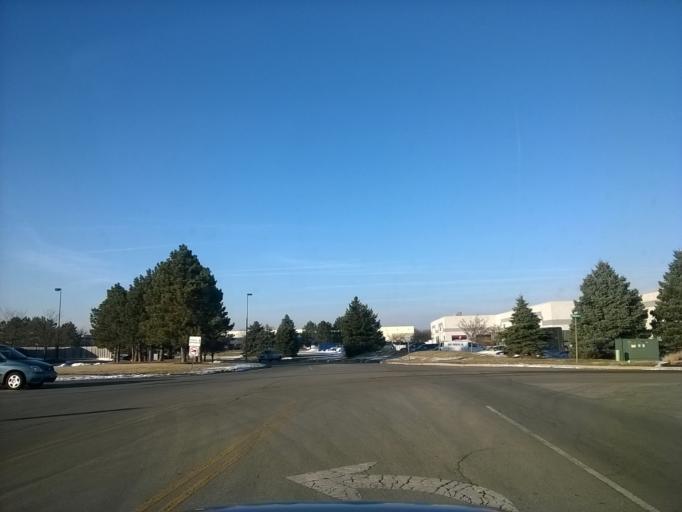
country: US
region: Indiana
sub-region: Hamilton County
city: Fishers
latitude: 39.9291
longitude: -86.0192
